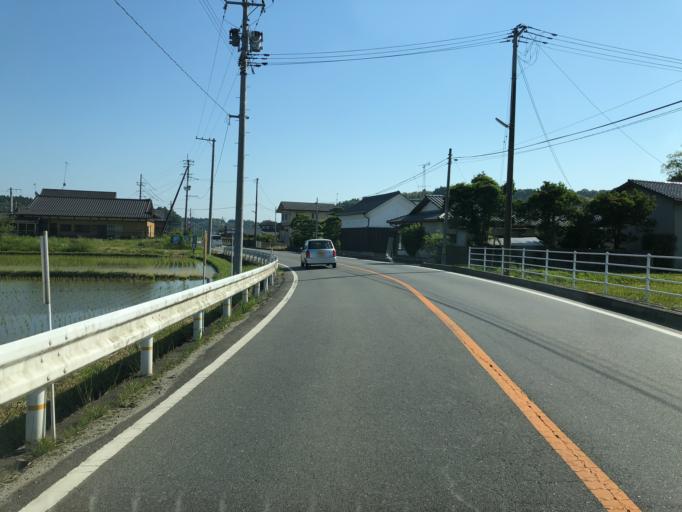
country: JP
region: Fukushima
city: Iwaki
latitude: 36.9352
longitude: 140.7982
